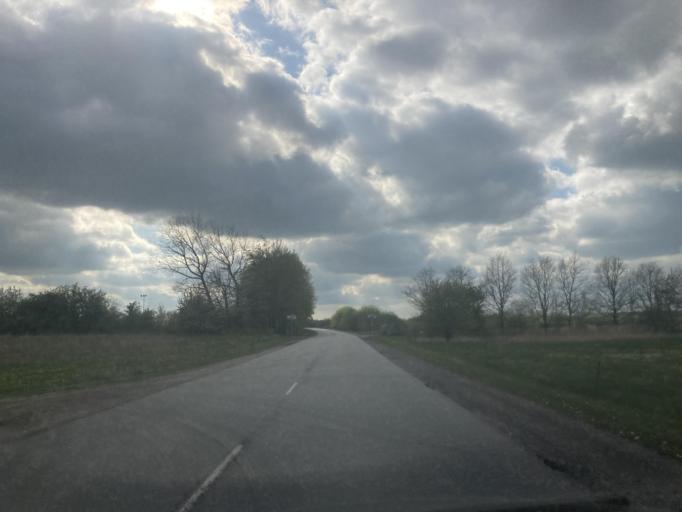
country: DK
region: Zealand
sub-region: Greve Kommune
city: Tune
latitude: 55.5999
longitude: 12.1728
